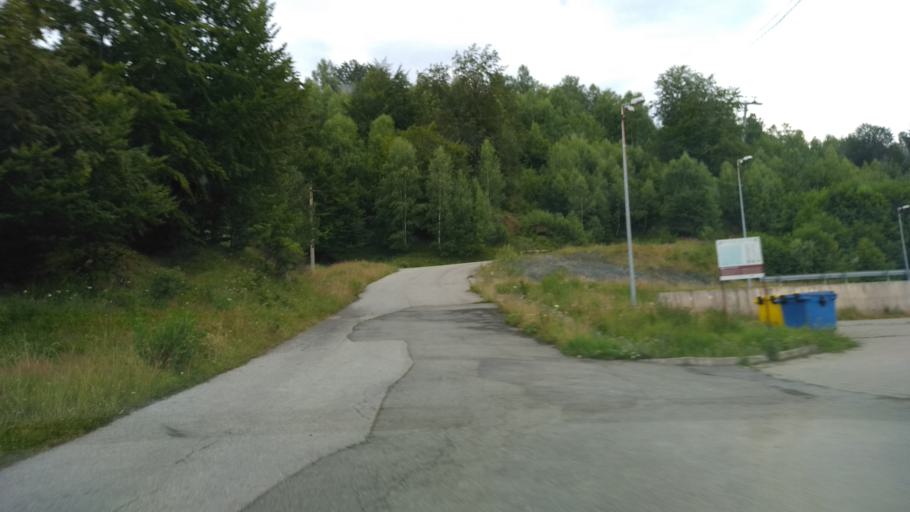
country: RO
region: Hunedoara
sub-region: Municipiul  Vulcan
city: Jiu-Paroseni
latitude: 45.3542
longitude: 23.2909
